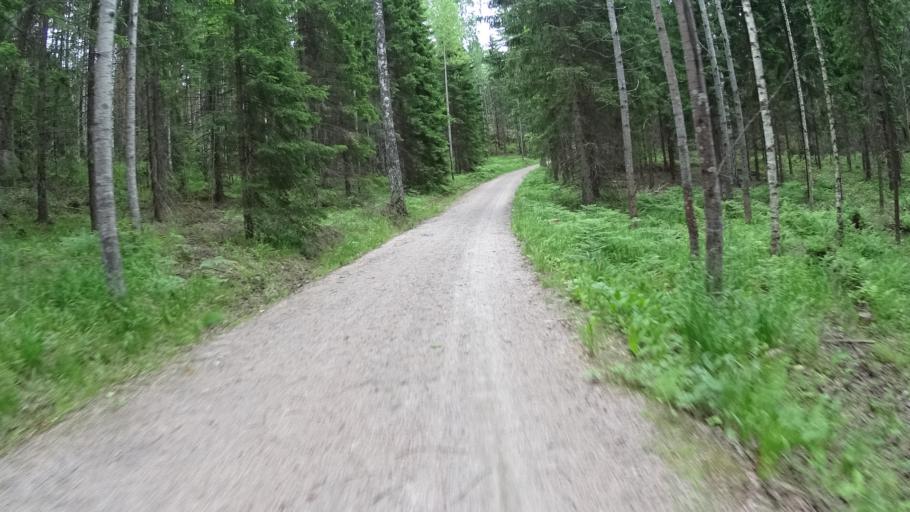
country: FI
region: Uusimaa
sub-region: Helsinki
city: Espoo
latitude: 60.2852
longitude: 24.5998
